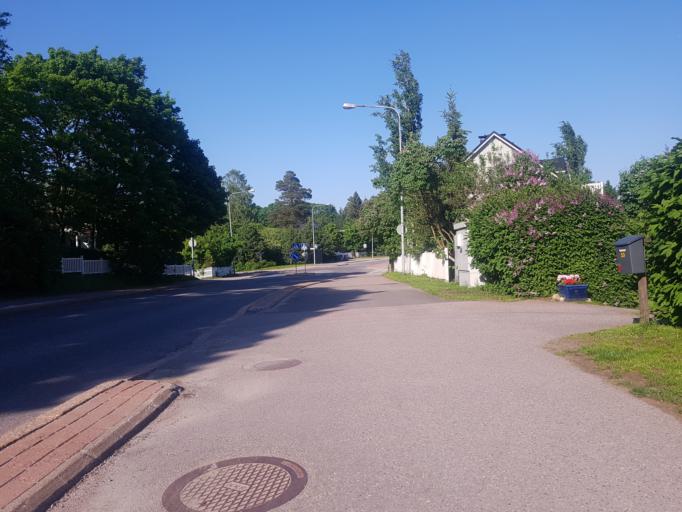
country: FI
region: Uusimaa
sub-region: Helsinki
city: Vantaa
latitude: 60.2611
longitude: 25.0039
